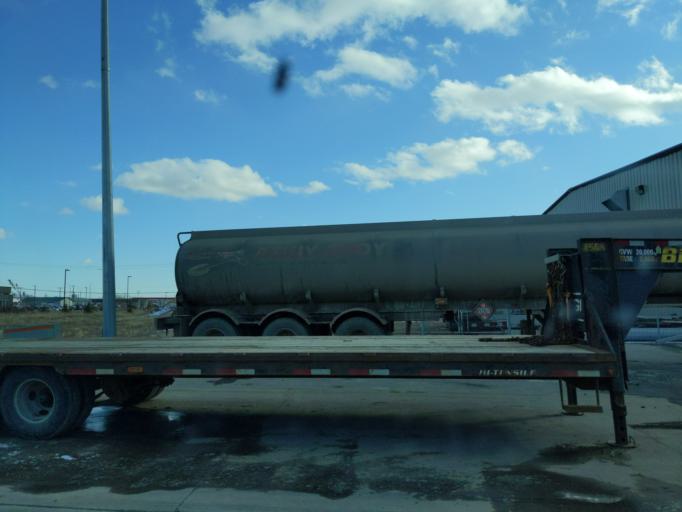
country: CA
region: Saskatchewan
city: Lloydminster
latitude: 53.2802
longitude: -109.9773
